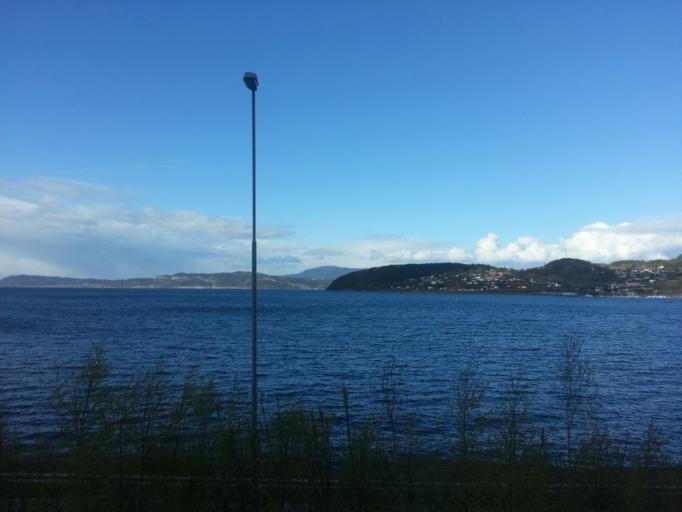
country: NO
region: Sor-Trondelag
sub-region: Malvik
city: Hommelvik
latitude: 63.4122
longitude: 10.7869
